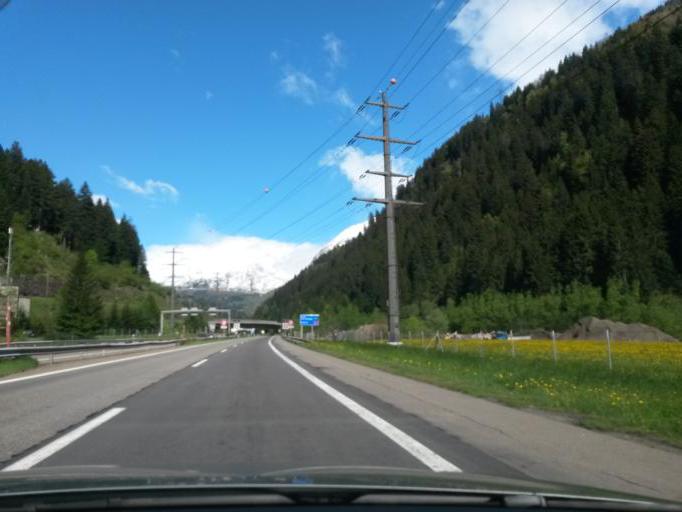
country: CH
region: Ticino
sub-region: Leventina District
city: Airolo
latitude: 46.5165
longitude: 8.6602
